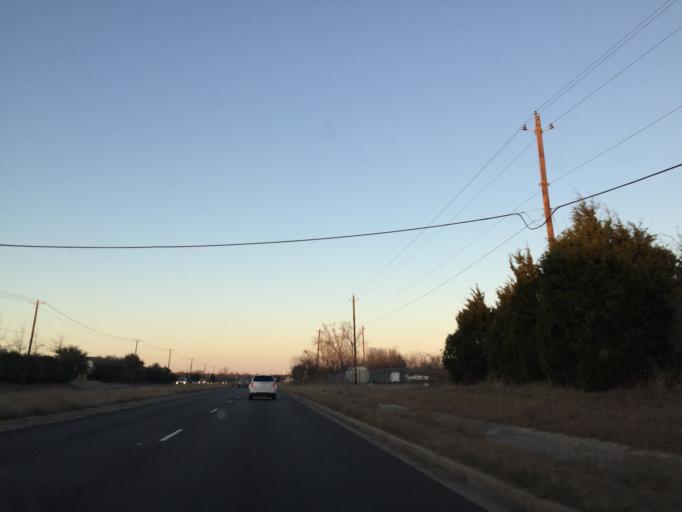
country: US
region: Texas
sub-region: Travis County
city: Pflugerville
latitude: 30.4177
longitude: -97.6306
